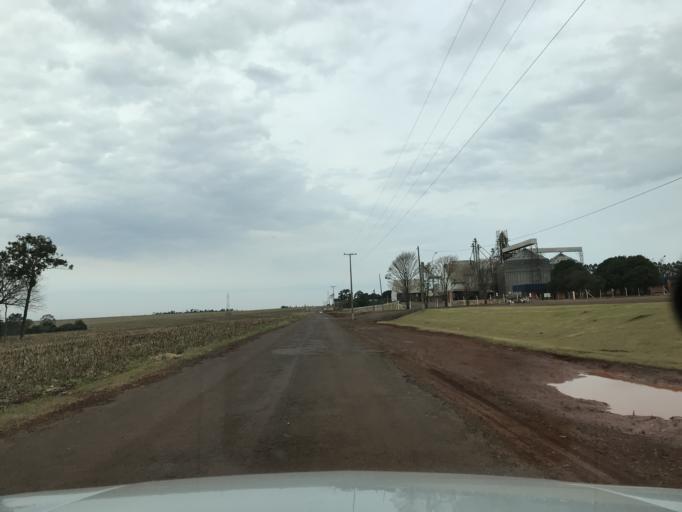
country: BR
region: Parana
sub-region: Palotina
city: Palotina
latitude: -24.2848
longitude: -53.8000
